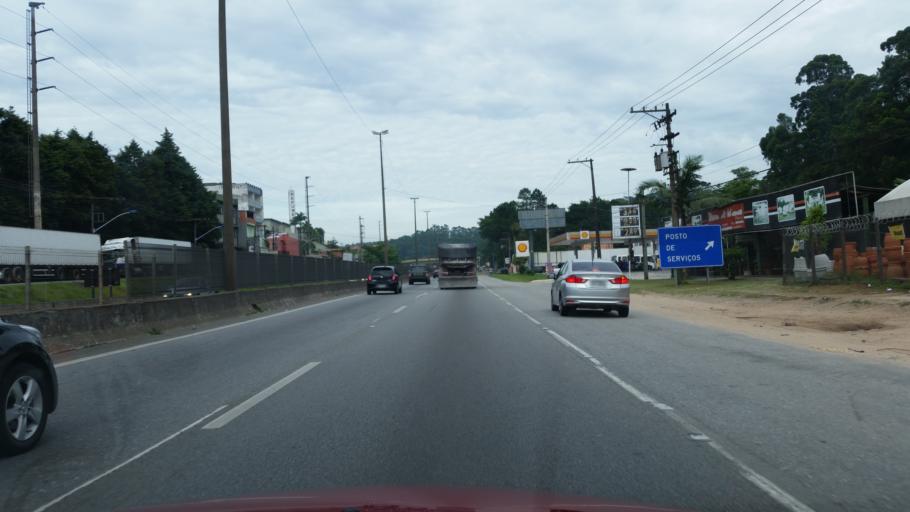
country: BR
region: Sao Paulo
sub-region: Taboao Da Serra
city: Taboao da Serra
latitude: -23.6180
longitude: -46.7986
